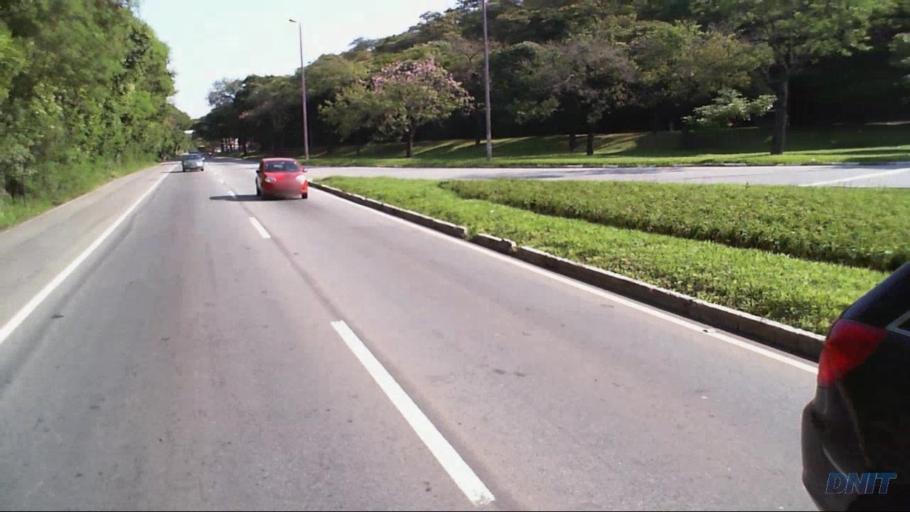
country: BR
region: Minas Gerais
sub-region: Ipatinga
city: Ipatinga
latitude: -19.4994
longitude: -42.5660
